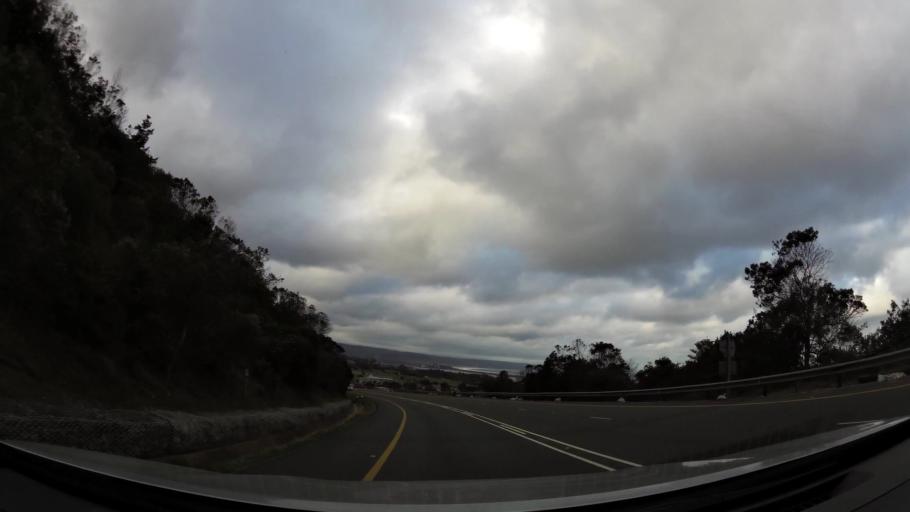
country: ZA
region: Western Cape
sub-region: Eden District Municipality
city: Plettenberg Bay
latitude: -34.0437
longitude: 23.3671
